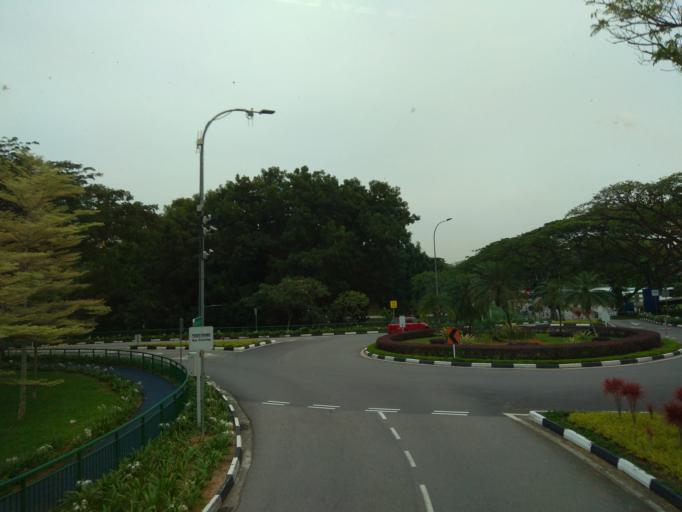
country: MY
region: Johor
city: Johor Bahru
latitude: 1.3498
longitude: 103.6848
